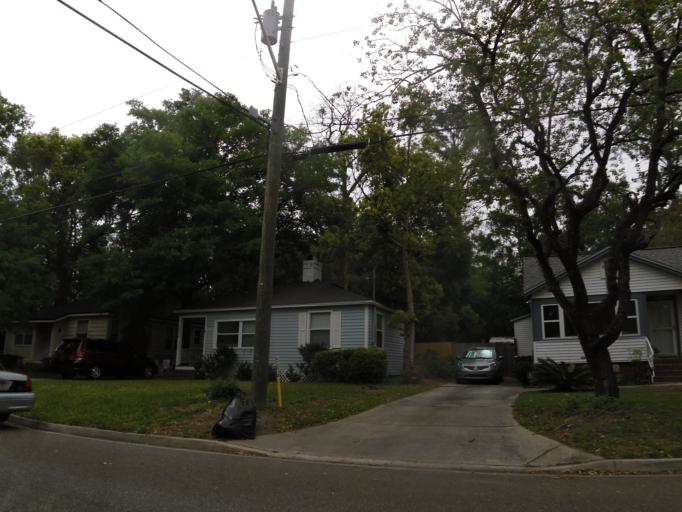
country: US
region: Florida
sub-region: Duval County
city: Jacksonville
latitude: 30.3054
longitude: -81.6497
